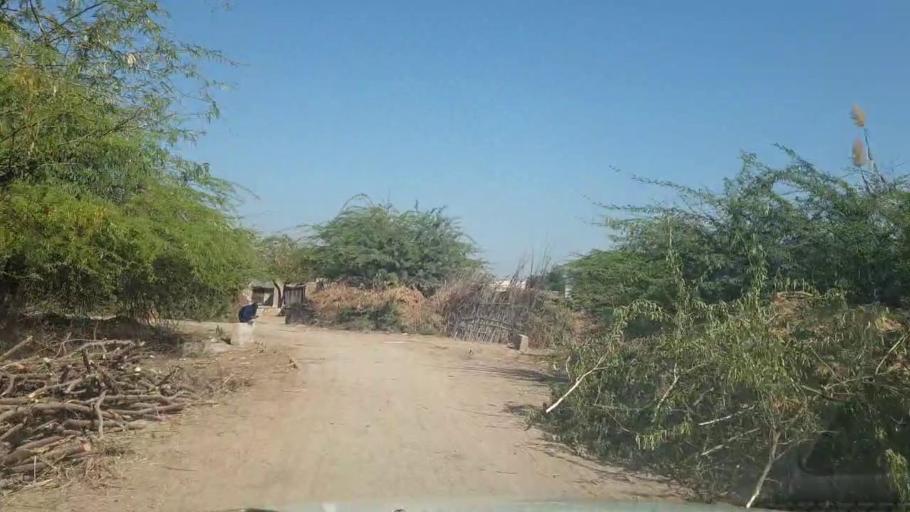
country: PK
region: Sindh
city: Mirpur Khas
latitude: 25.5176
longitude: 69.1495
